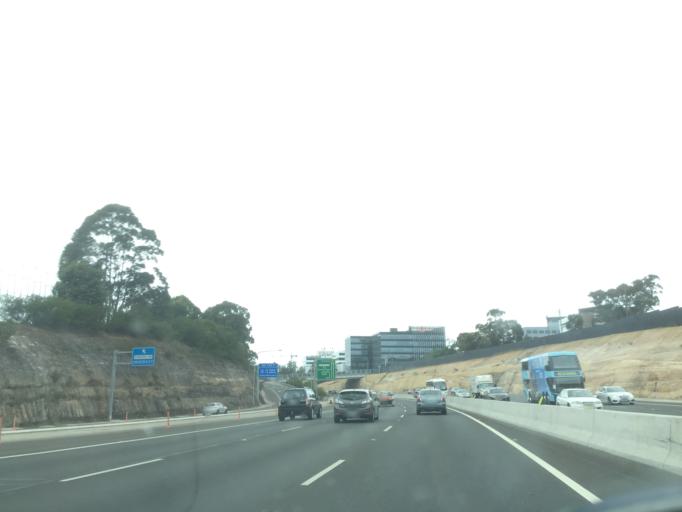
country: AU
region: New South Wales
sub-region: Ryde
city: Macquarie Park
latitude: -33.7704
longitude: 151.1168
